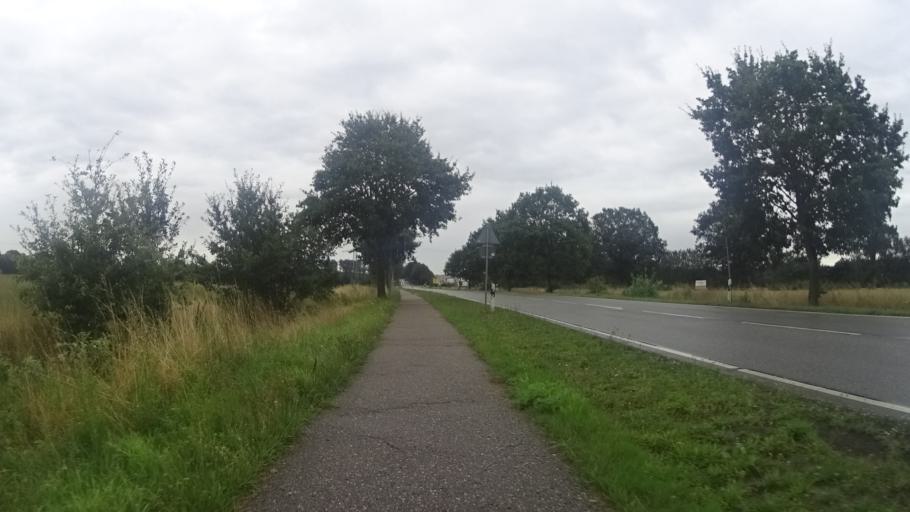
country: DE
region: Schleswig-Holstein
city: Kiebitzreihe
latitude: 53.7808
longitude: 9.6426
